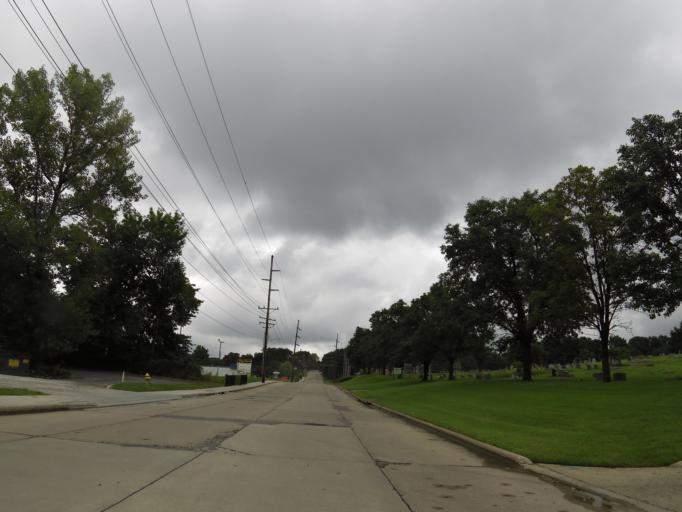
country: US
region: Missouri
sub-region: Cape Girardeau County
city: Cape Girardeau
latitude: 37.3161
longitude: -89.5469
